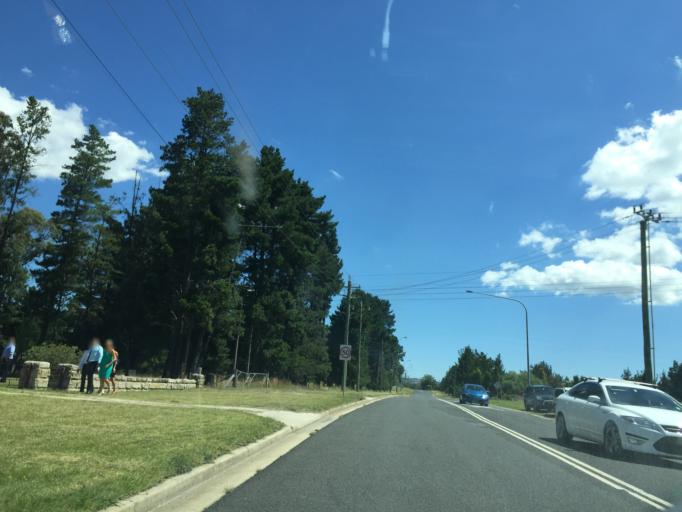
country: AU
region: New South Wales
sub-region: Lithgow
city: Lithgow
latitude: -33.4005
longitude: 150.0776
